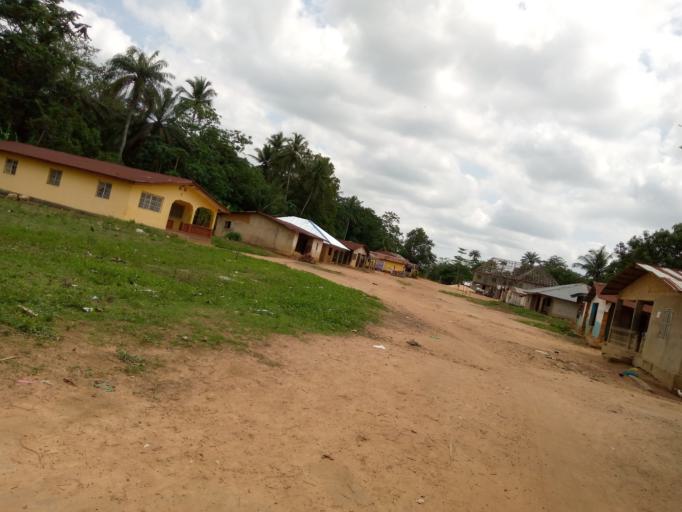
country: SL
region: Western Area
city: Waterloo
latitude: 8.4033
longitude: -12.9493
